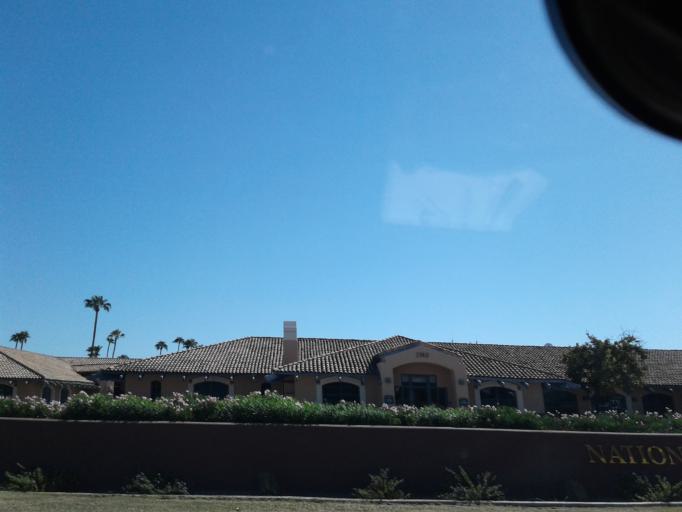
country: US
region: Arizona
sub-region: Maricopa County
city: Paradise Valley
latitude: 33.5197
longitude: -111.9258
